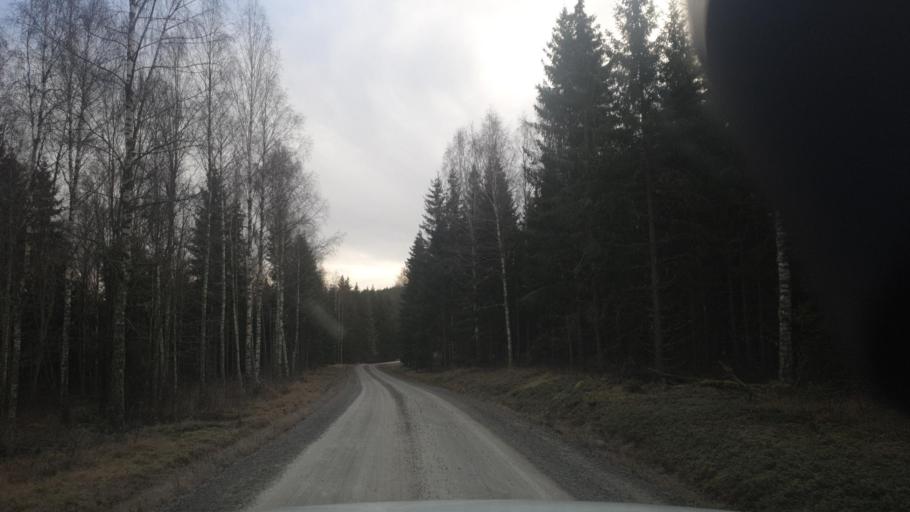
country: SE
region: Vaermland
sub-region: Eda Kommun
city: Amotfors
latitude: 59.8599
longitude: 12.5092
